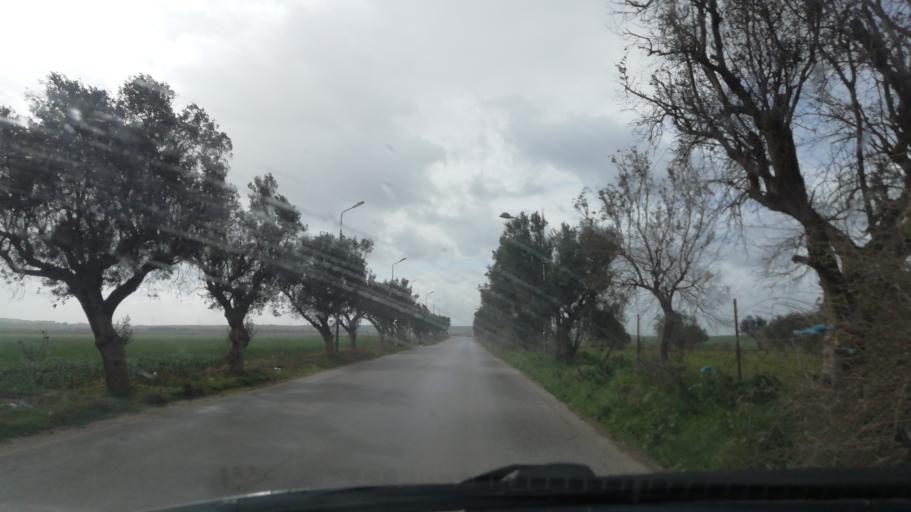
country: DZ
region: Oran
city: Sidi ech Chahmi
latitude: 35.6503
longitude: -0.5233
